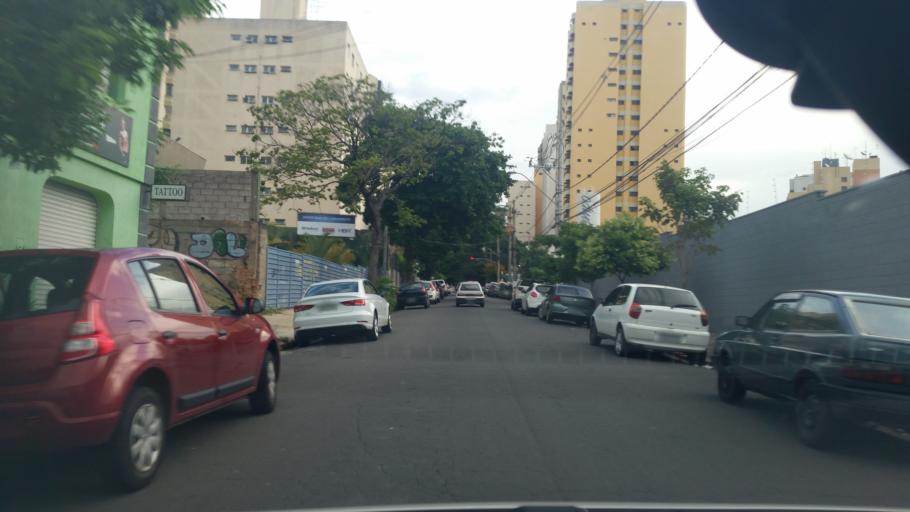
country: BR
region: Sao Paulo
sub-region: Campinas
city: Campinas
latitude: -22.8917
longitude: -47.0580
